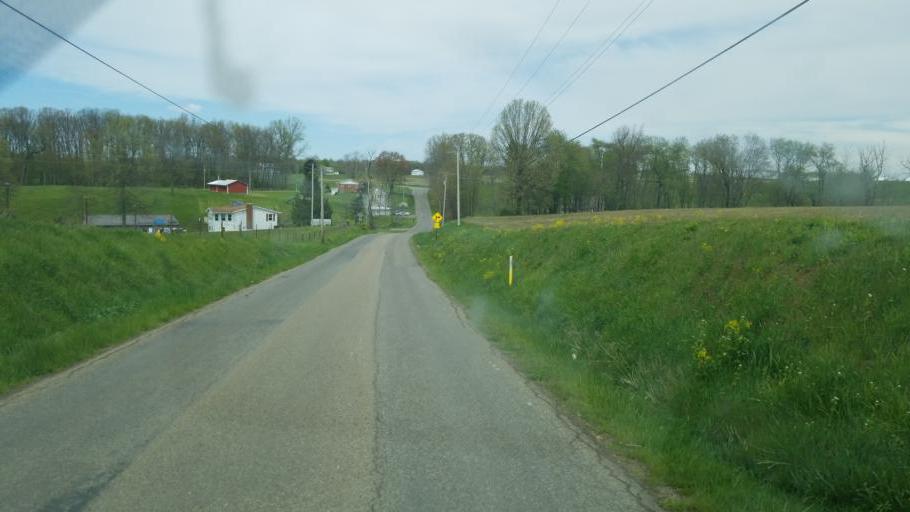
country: US
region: Ohio
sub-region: Wayne County
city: Apple Creek
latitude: 40.7309
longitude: -81.9078
